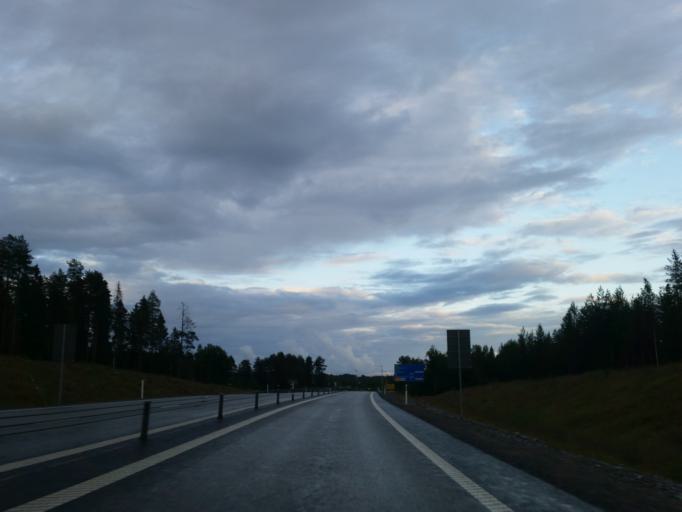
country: SE
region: Vaesterbotten
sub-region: Umea Kommun
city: Umea
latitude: 63.8522
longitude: 20.2884
